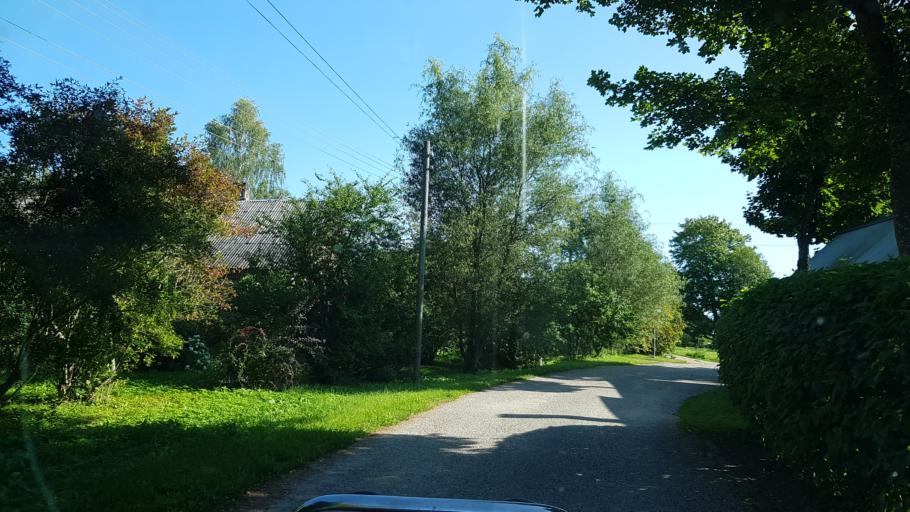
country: EE
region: Vorumaa
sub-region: Voru linn
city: Voru
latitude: 57.7330
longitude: 26.9208
